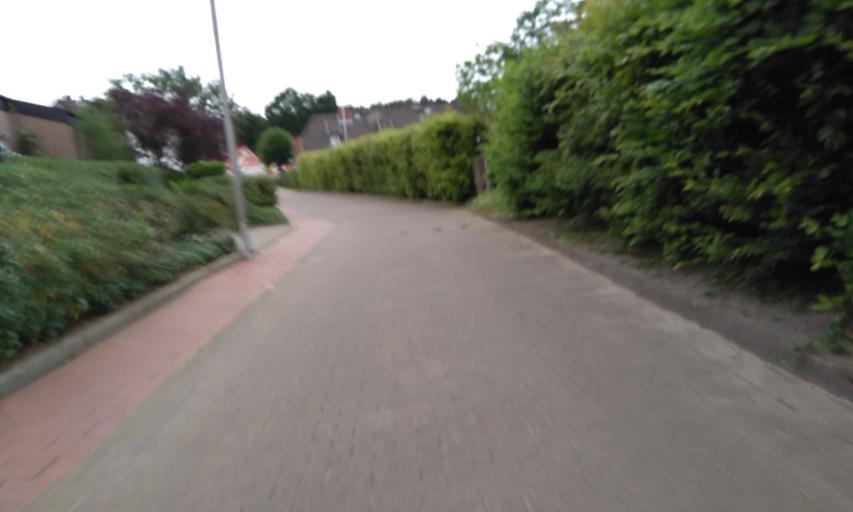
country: DE
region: Lower Saxony
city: Harsefeld
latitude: 53.4573
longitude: 9.5020
